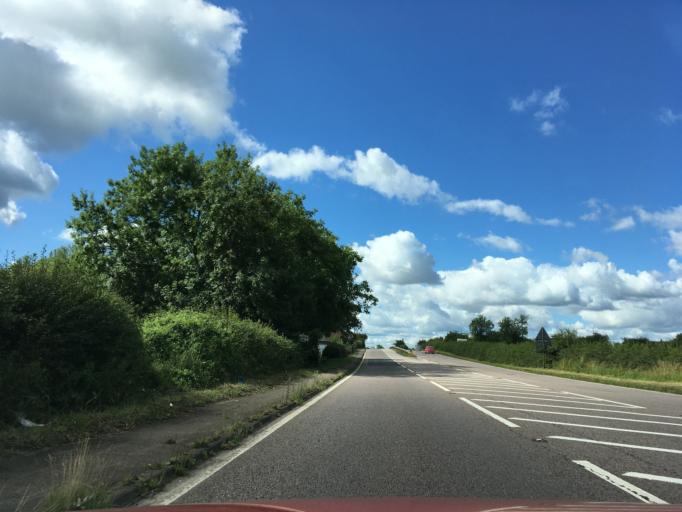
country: GB
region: England
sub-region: Gloucestershire
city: Newent
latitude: 51.8432
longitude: -2.3555
